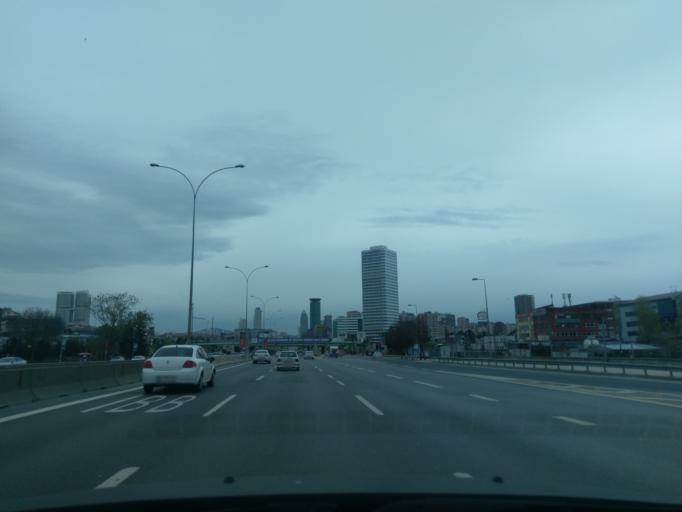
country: TR
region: Istanbul
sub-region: Atasehir
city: Atasehir
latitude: 40.9940
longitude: 29.0693
